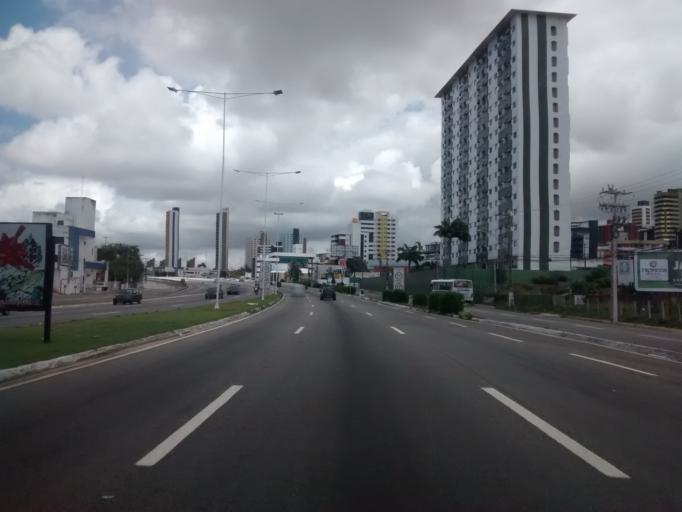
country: BR
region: Rio Grande do Norte
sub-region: Natal
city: Natal
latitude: -5.8321
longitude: -35.2122
